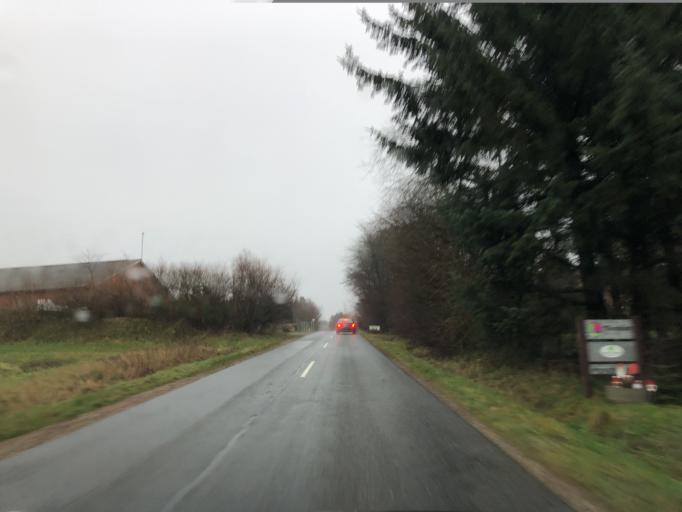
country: DK
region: Central Jutland
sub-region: Holstebro Kommune
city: Ulfborg
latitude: 56.2010
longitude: 8.4122
